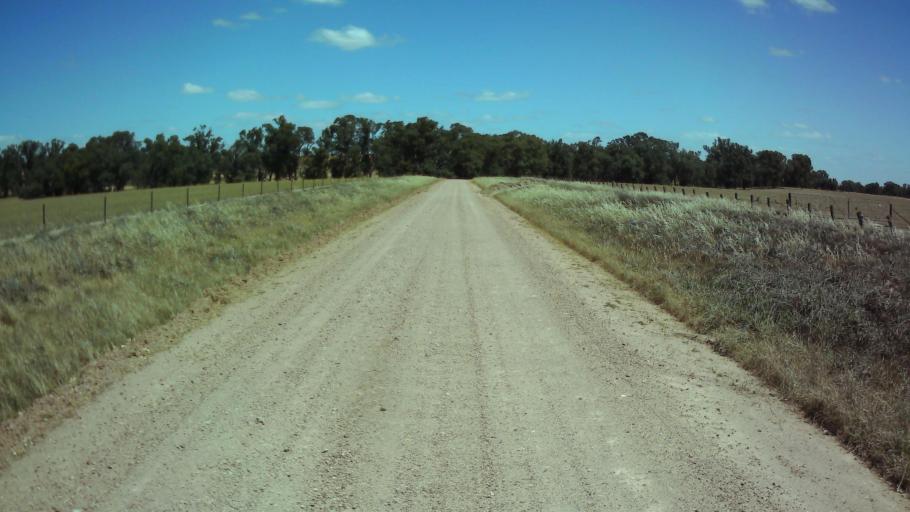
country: AU
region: New South Wales
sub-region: Weddin
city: Grenfell
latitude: -33.9305
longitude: 148.3345
